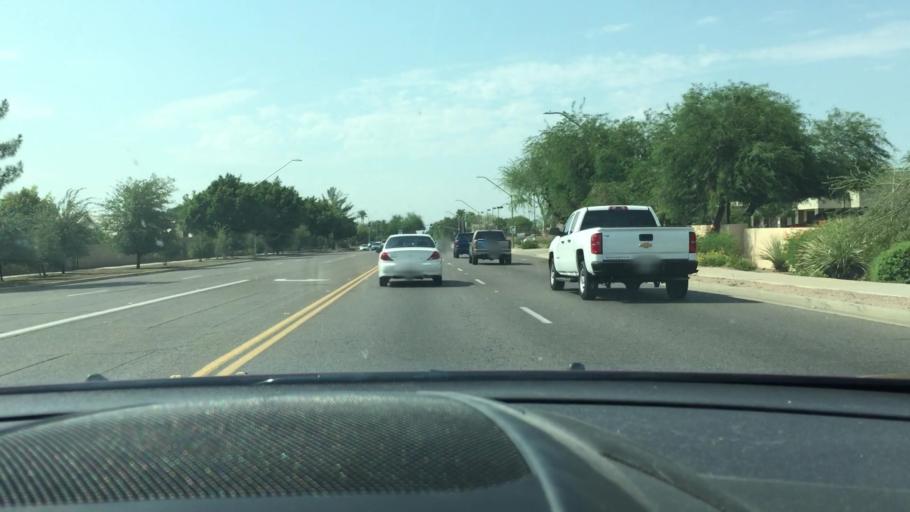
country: US
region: Arizona
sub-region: Maricopa County
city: Peoria
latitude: 33.6843
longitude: -112.2031
